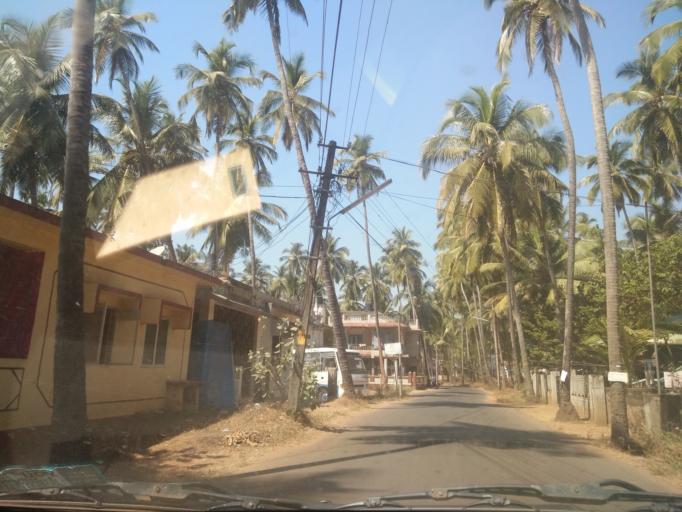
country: IN
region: Goa
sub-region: North Goa
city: Morjim
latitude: 15.6325
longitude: 73.7434
